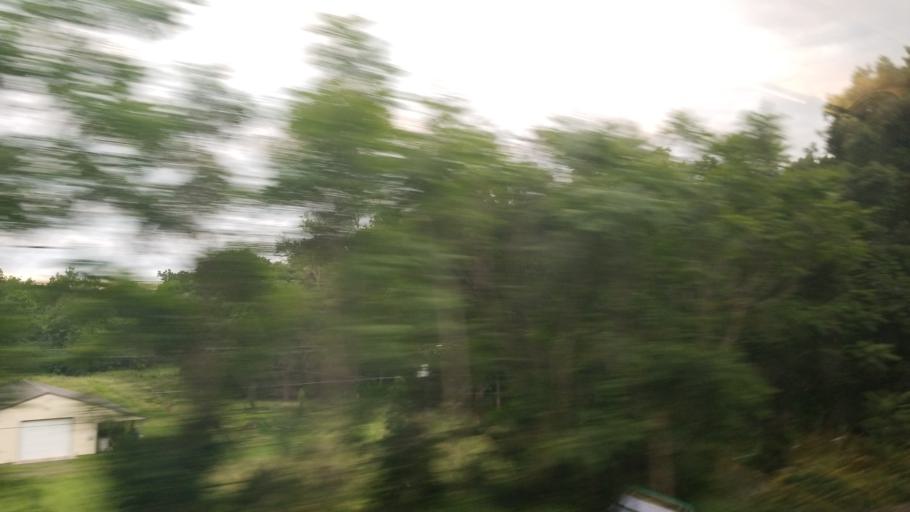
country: US
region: Virginia
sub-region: Culpeper County
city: Culpeper
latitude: 38.4212
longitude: -78.0031
